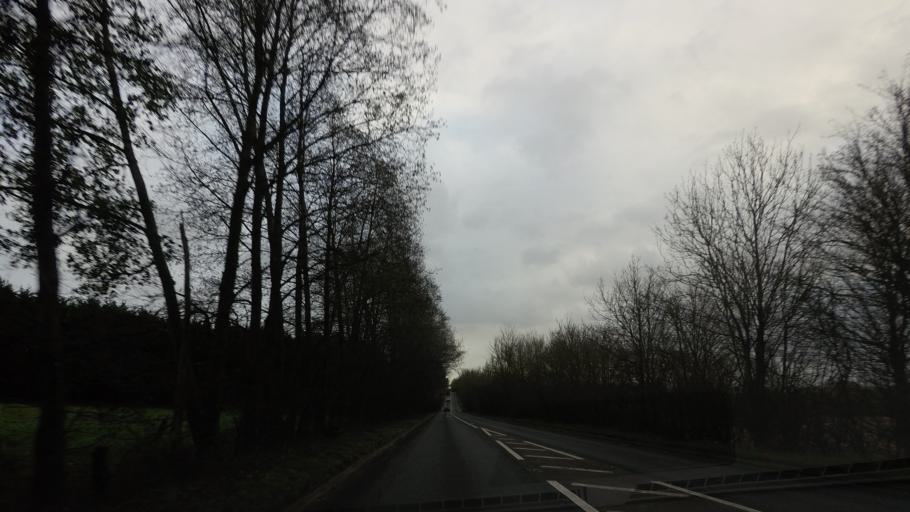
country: GB
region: England
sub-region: Kent
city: East Peckham
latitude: 51.2391
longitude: 0.3794
